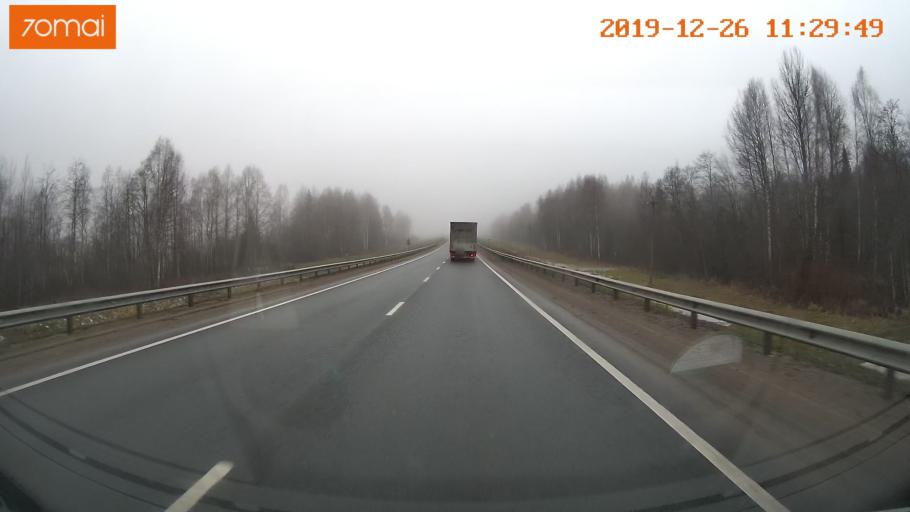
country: RU
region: Vologda
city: Chebsara
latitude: 59.1622
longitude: 38.7863
